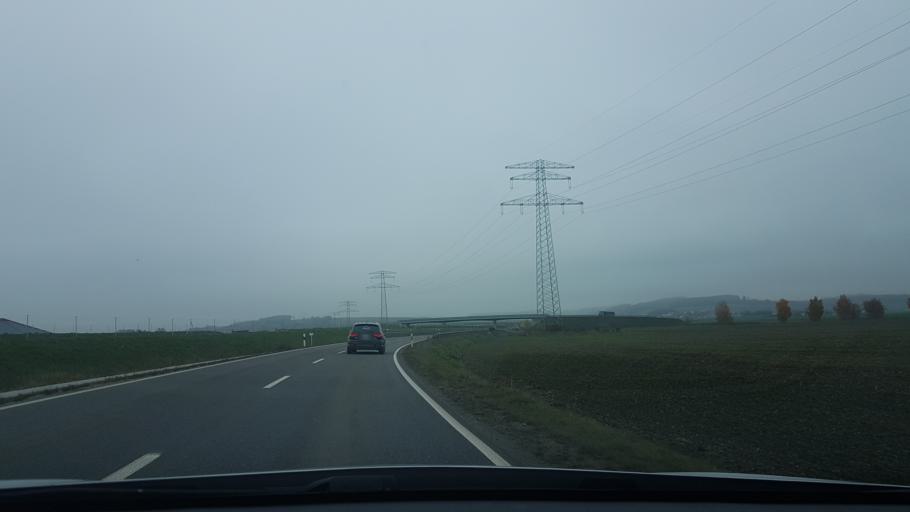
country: DE
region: Bavaria
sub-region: Lower Bavaria
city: Essenbach
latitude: 48.6076
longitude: 12.2307
